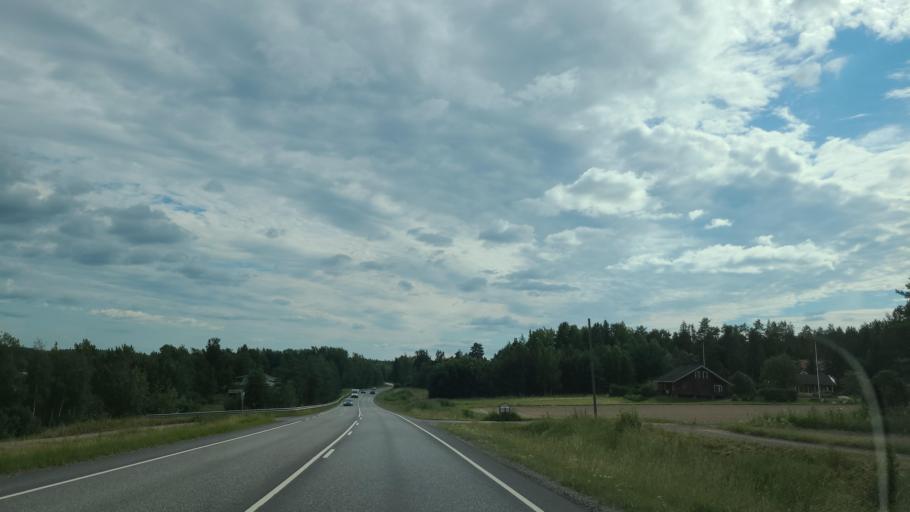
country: FI
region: Varsinais-Suomi
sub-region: Turku
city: Merimasku
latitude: 60.4359
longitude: 21.8957
